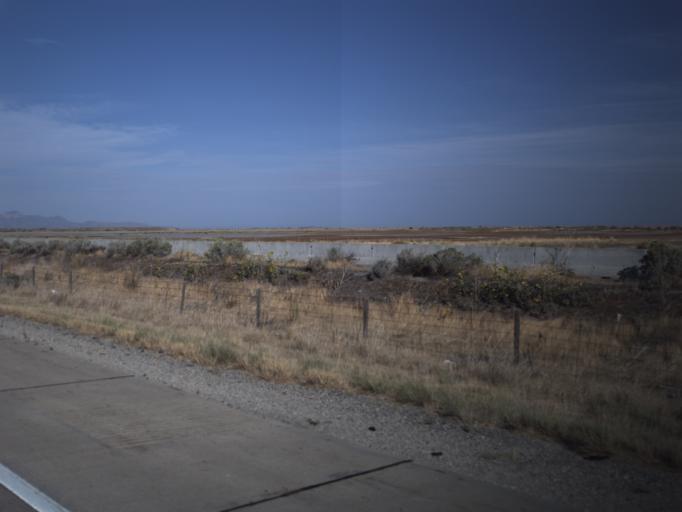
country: US
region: Utah
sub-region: Salt Lake County
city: Magna
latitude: 40.7710
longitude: -112.1253
